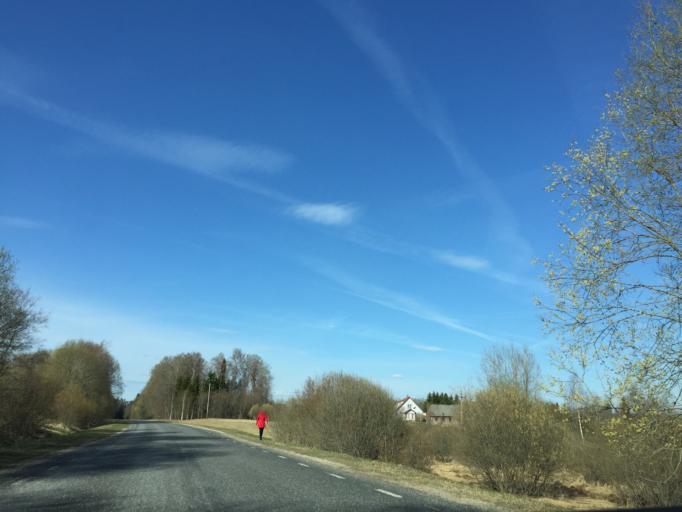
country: EE
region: Vorumaa
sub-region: Antsla vald
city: Vana-Antsla
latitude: 57.9983
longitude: 26.4235
